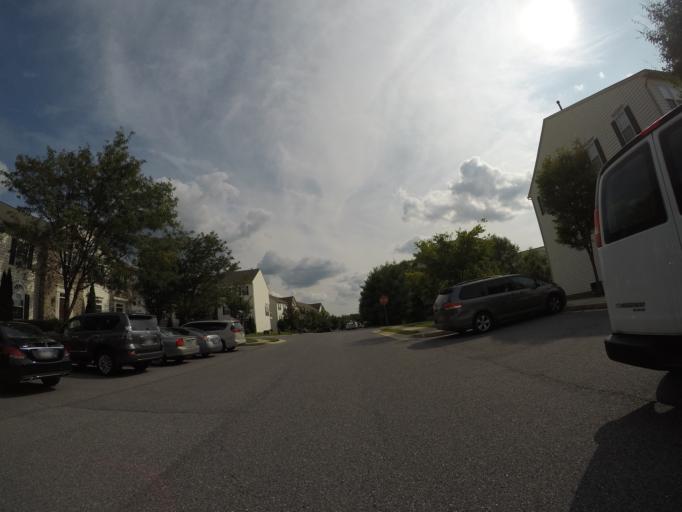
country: US
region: Maryland
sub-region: Howard County
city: Columbia
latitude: 39.3097
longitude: -76.8886
